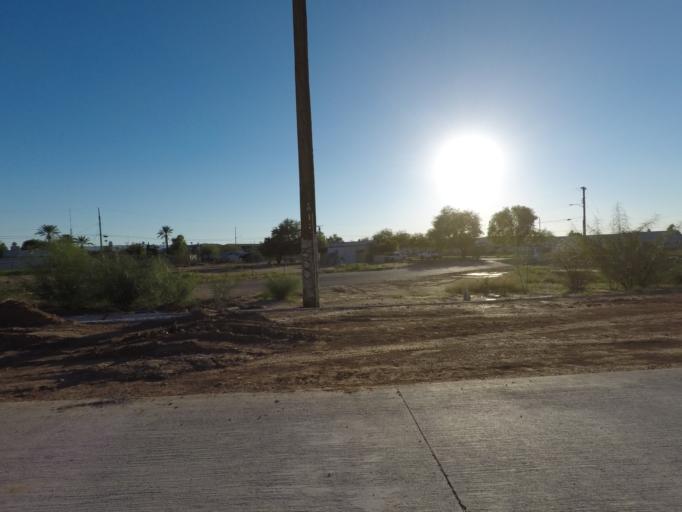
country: US
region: Arizona
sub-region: Maricopa County
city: Tempe Junction
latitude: 33.4551
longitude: -112.0014
